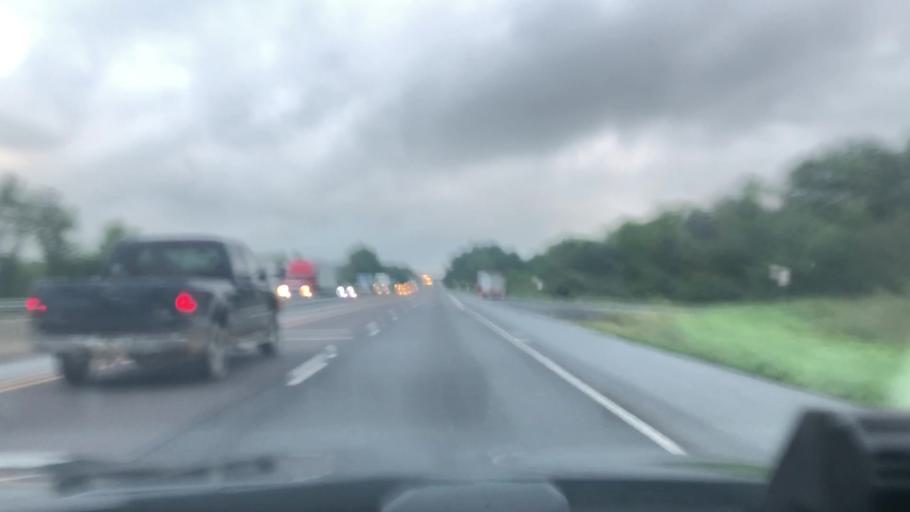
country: US
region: Pennsylvania
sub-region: Schuylkill County
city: Lake Wynonah
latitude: 40.5081
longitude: -76.1466
